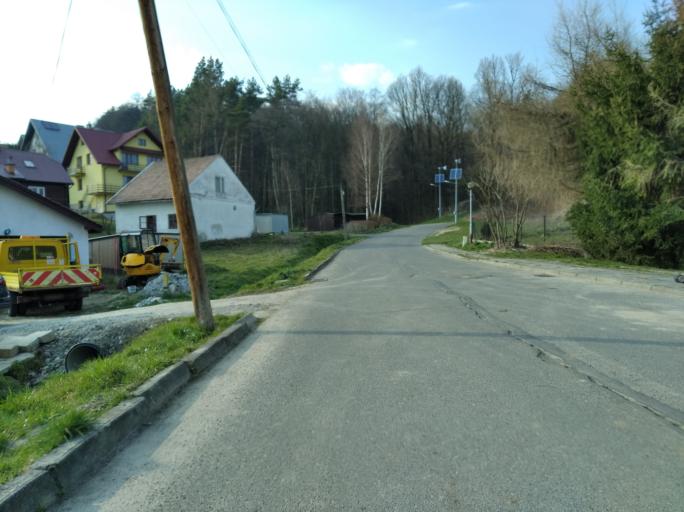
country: PL
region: Subcarpathian Voivodeship
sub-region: Powiat strzyzowski
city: Strzyzow
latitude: 49.8756
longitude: 21.7907
